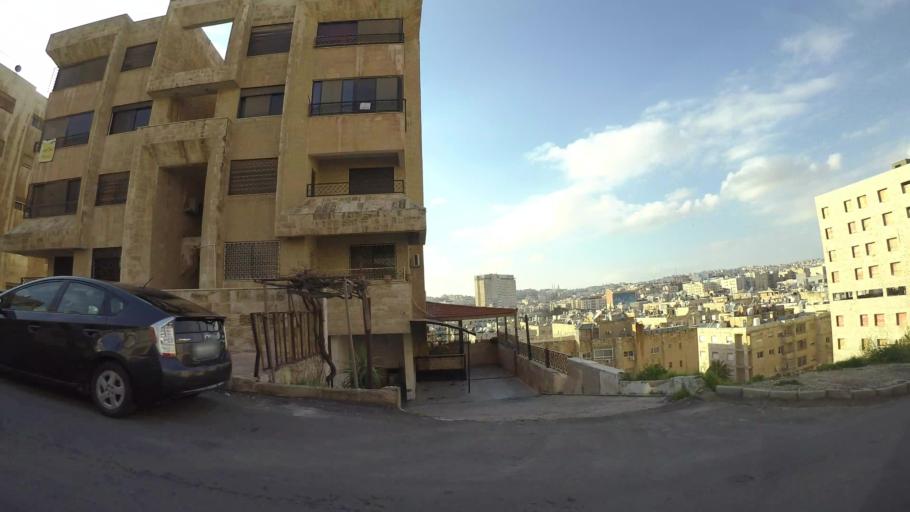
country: JO
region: Amman
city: Al Jubayhah
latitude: 31.9831
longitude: 35.8689
